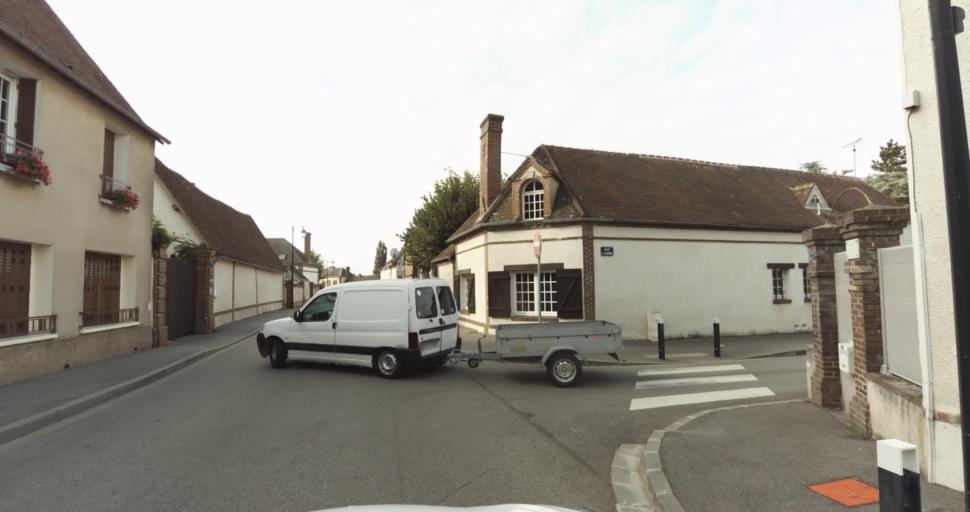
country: FR
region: Haute-Normandie
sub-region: Departement de l'Eure
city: Saint-Germain-sur-Avre
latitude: 48.8209
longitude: 1.2668
